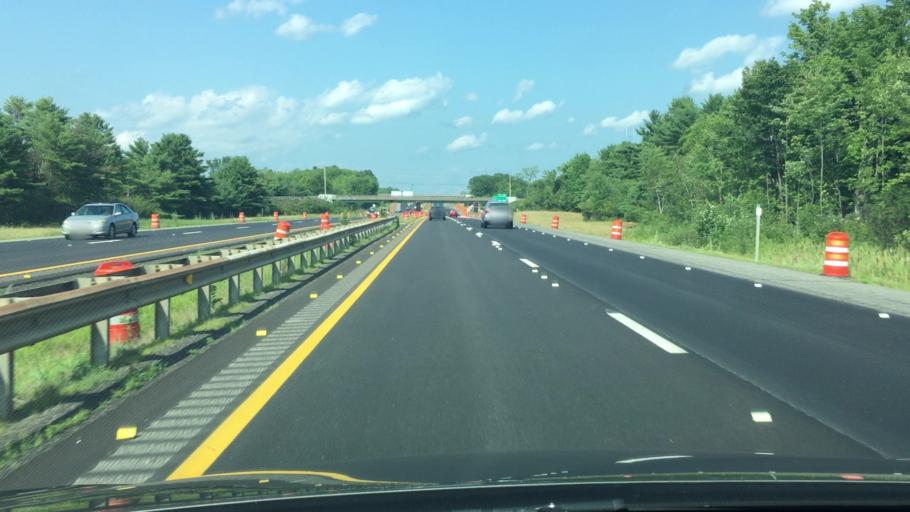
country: US
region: Maine
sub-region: Kennebec County
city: Gardiner
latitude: 44.2061
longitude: -69.8349
